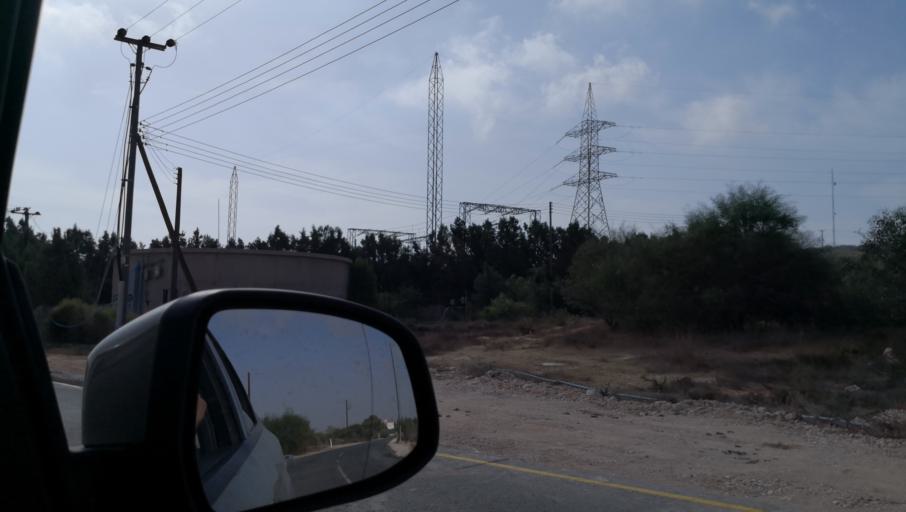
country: CY
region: Ammochostos
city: Protaras
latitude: 35.0146
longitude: 34.0311
